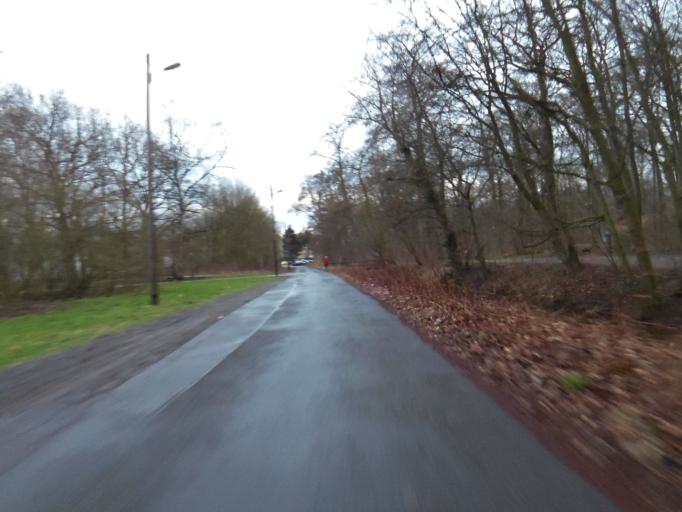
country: DE
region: Lower Saxony
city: Hannover
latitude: 52.3789
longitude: 9.7873
